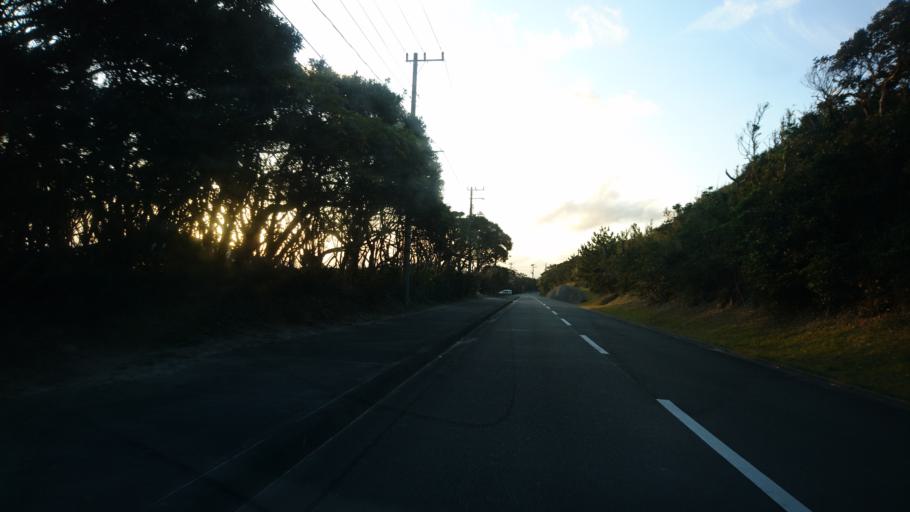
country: JP
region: Shizuoka
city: Shimoda
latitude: 34.3629
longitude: 139.2492
